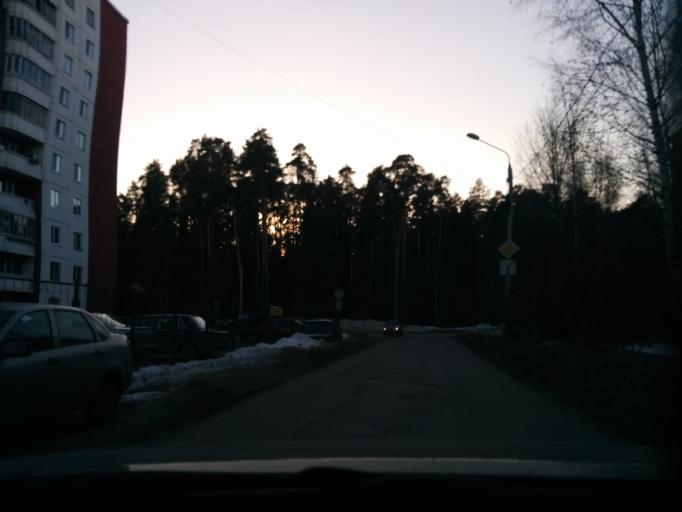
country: RU
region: Perm
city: Kondratovo
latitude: 58.0242
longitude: 56.0032
